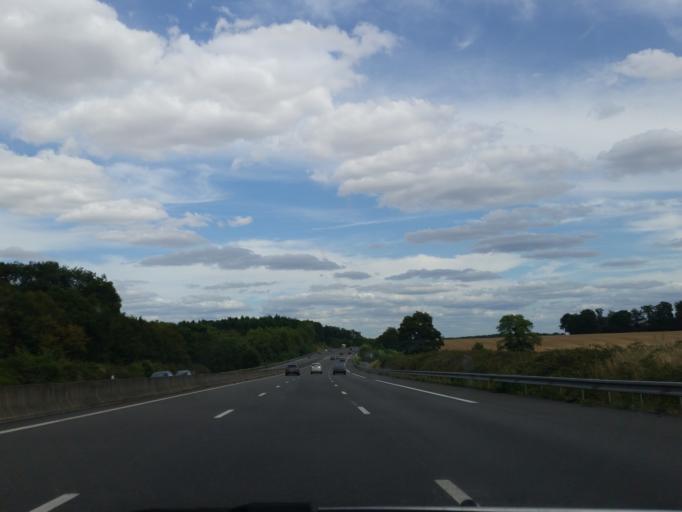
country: FR
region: Centre
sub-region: Departement du Loir-et-Cher
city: Saint-Sulpice-de-Pommeray
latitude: 47.6194
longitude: 1.2310
